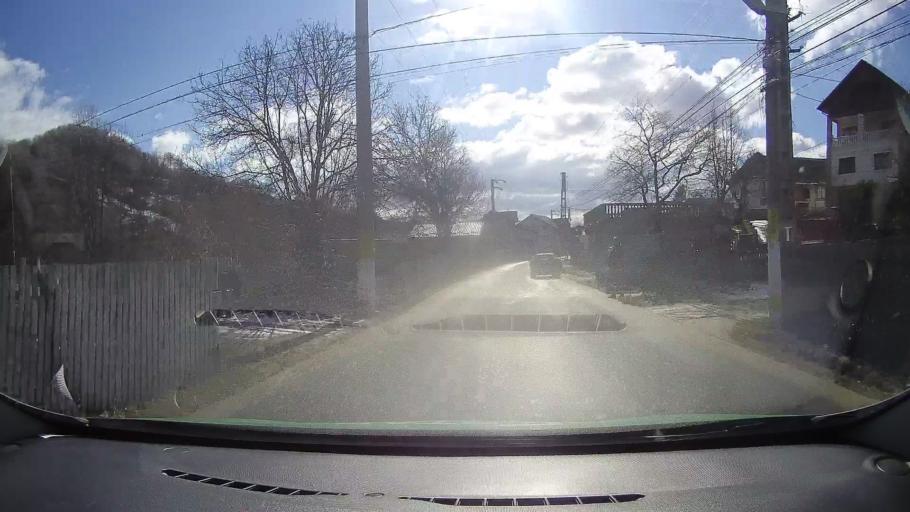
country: RO
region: Dambovita
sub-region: Comuna Runcu
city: Runcu
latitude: 45.1693
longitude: 25.3945
